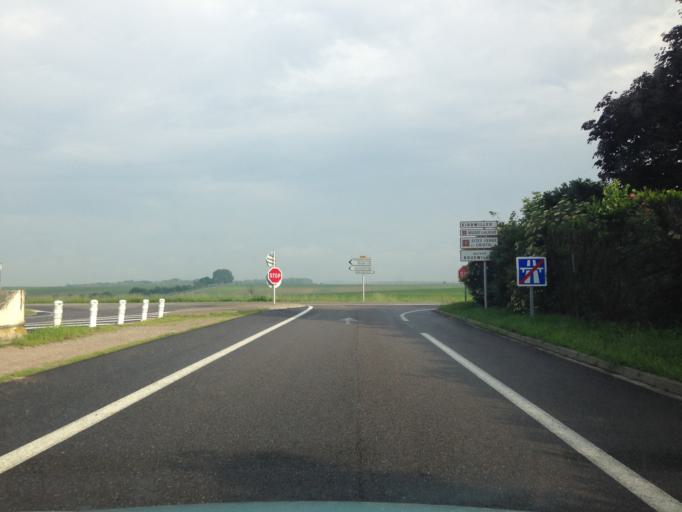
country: FR
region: Alsace
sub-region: Departement du Bas-Rhin
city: Schwindratzheim
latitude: 48.7709
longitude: 7.6001
